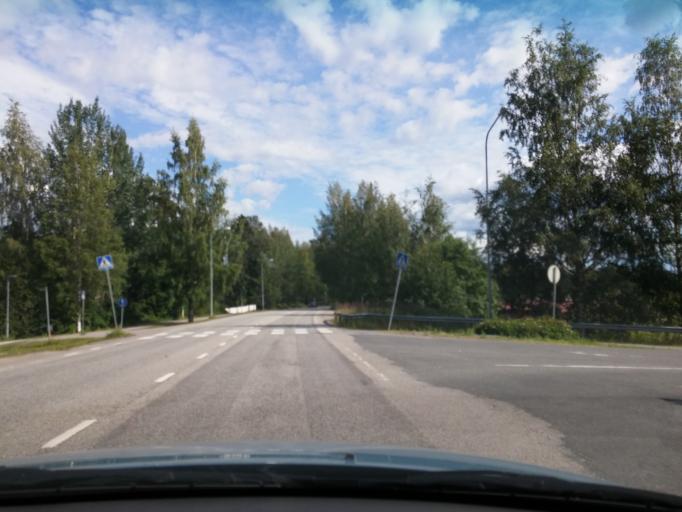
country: FI
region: Central Finland
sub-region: Keuruu
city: Keuruu
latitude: 62.2678
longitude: 24.6947
